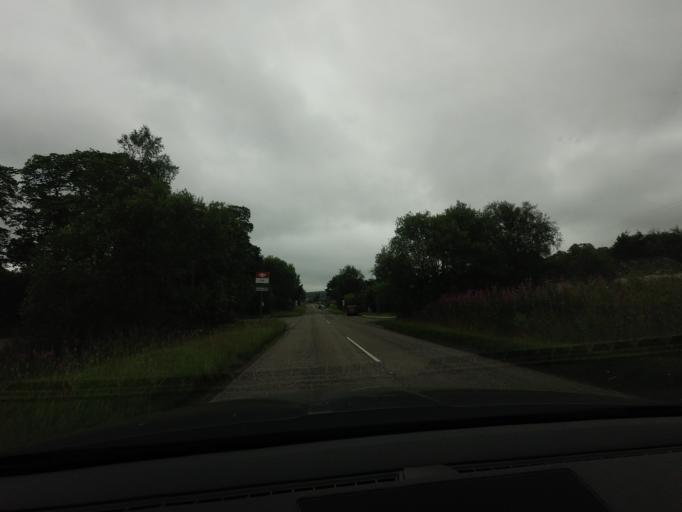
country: GB
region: Scotland
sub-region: Highland
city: Alness
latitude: 58.0024
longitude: -4.3981
